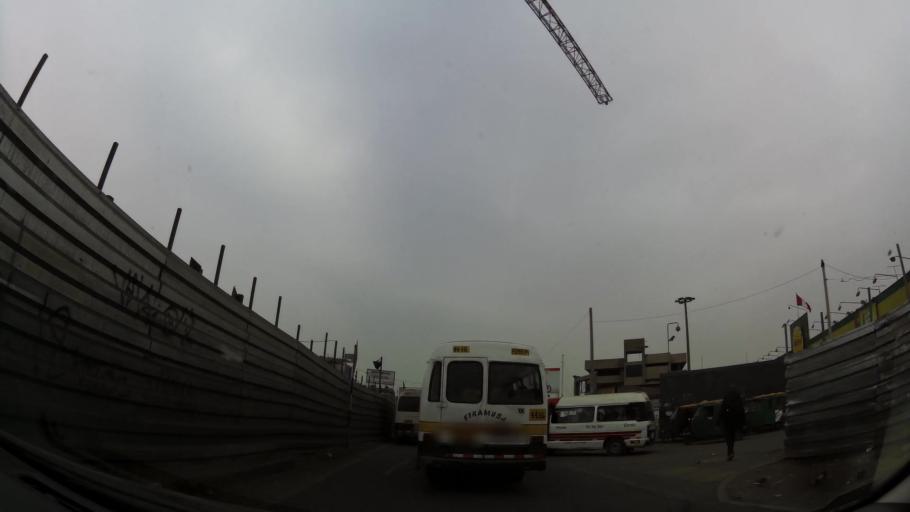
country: PE
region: Lima
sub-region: Lima
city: Vitarte
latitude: -12.0418
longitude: -76.9352
